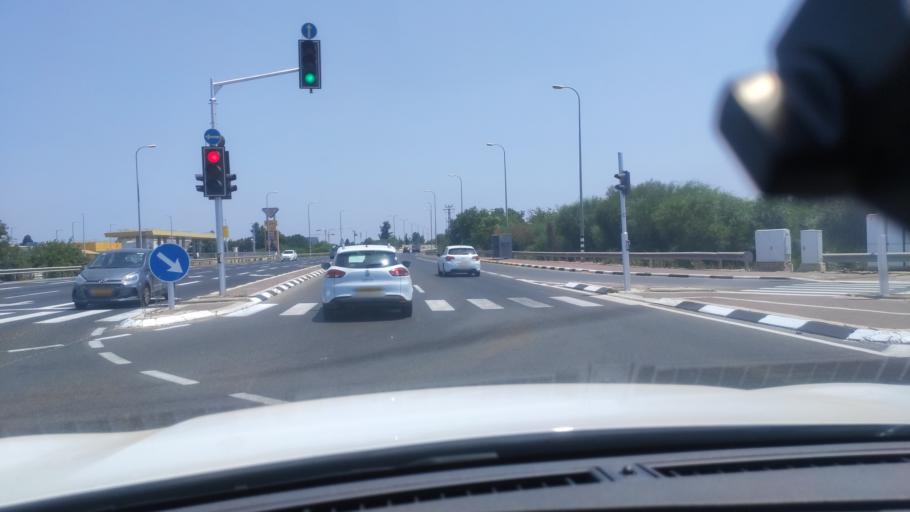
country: IL
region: Central District
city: Kfar Saba
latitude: 32.1514
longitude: 34.9212
